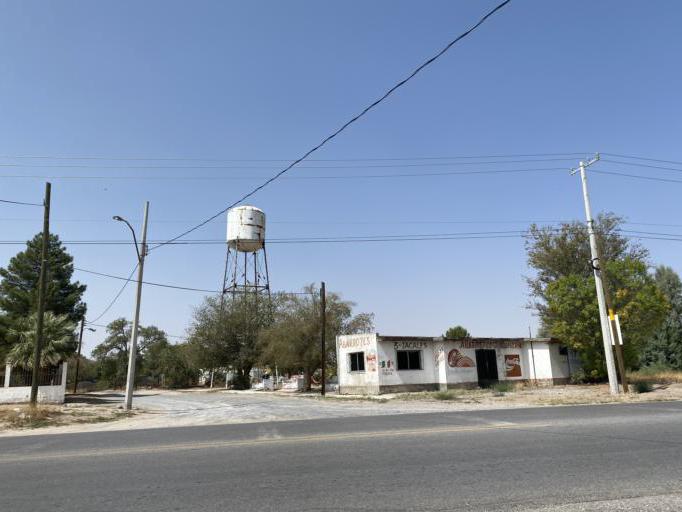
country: US
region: Texas
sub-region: El Paso County
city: Fabens
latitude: 31.4736
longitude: -106.2215
